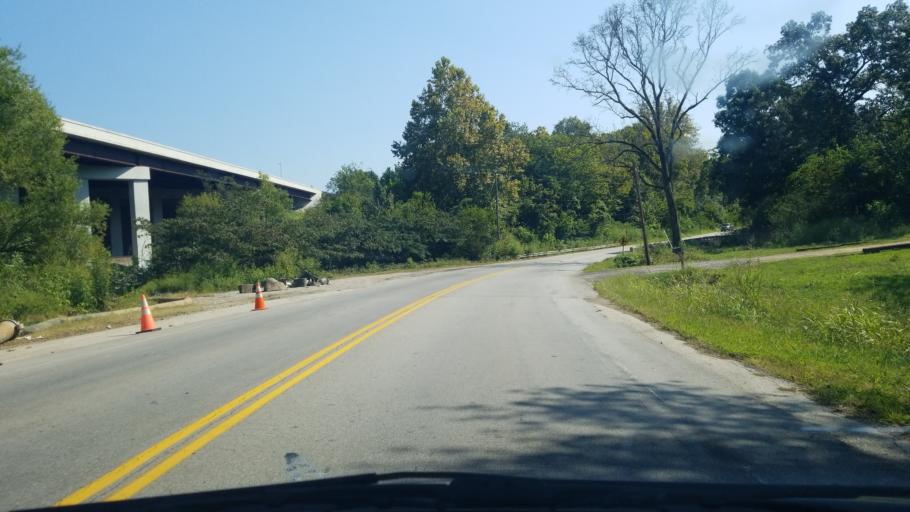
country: US
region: Tennessee
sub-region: Hamilton County
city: Harrison
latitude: 35.0695
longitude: -85.1191
